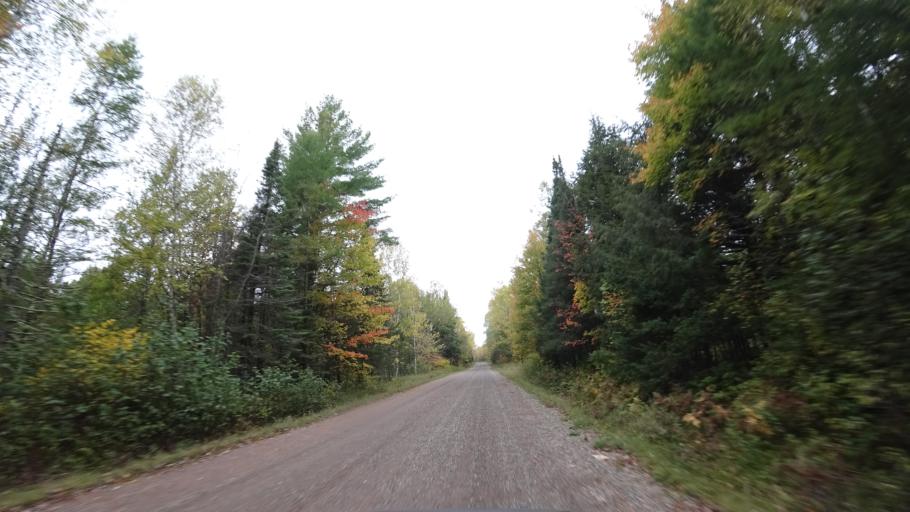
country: US
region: Wisconsin
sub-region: Sawyer County
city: Little Round Lake
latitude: 45.9707
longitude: -90.9813
